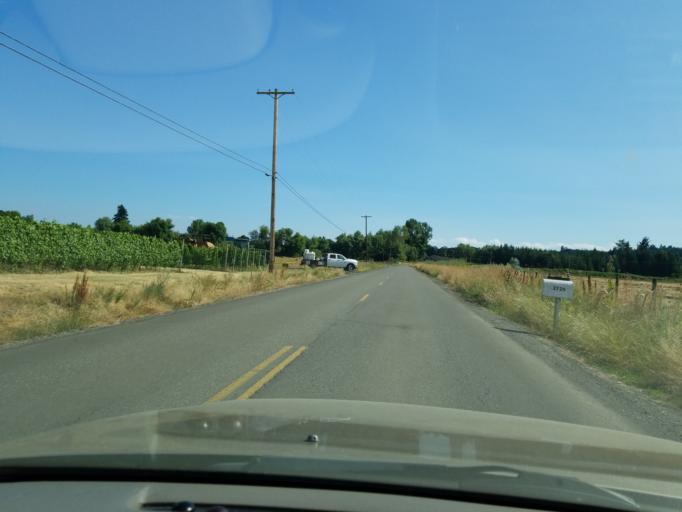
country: US
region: Oregon
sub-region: Yamhill County
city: McMinnville
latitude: 45.2340
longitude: -123.2310
